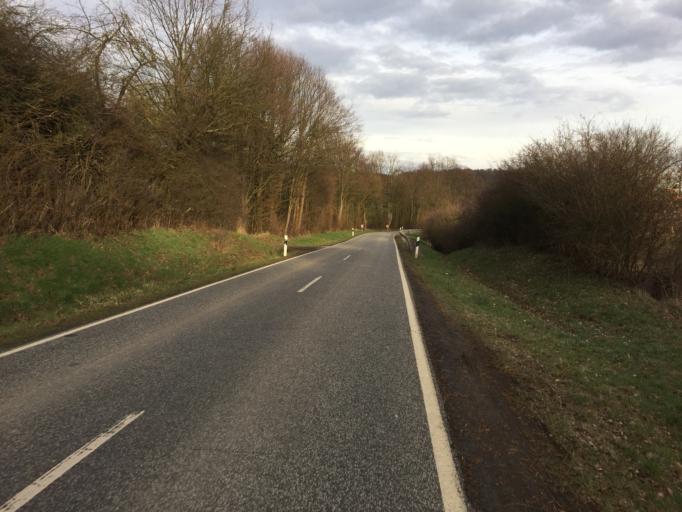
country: DE
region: Hesse
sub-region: Regierungsbezirk Giessen
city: Rabenau
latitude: 50.6828
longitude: 8.8535
